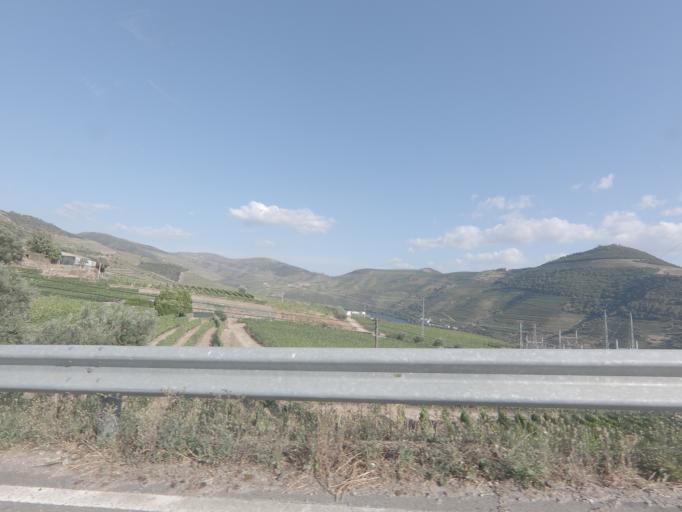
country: PT
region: Vila Real
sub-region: Sabrosa
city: Vilela
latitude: 41.1948
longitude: -7.5422
